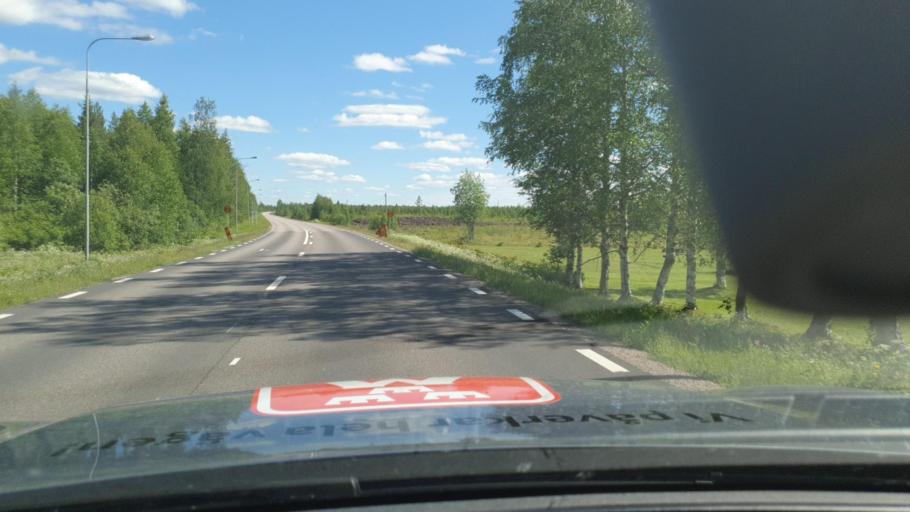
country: SE
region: Norrbotten
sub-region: Pajala Kommun
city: Pajala
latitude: 67.2000
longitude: 23.4119
